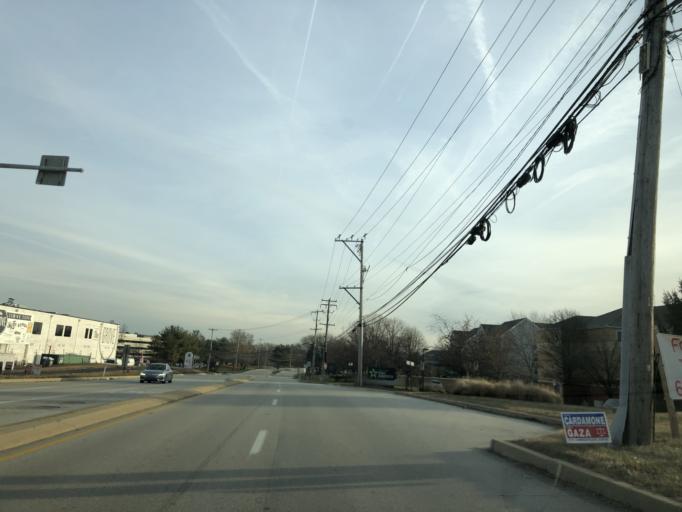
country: US
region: Pennsylvania
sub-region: Chester County
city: Malvern
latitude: 40.0526
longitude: -75.5268
